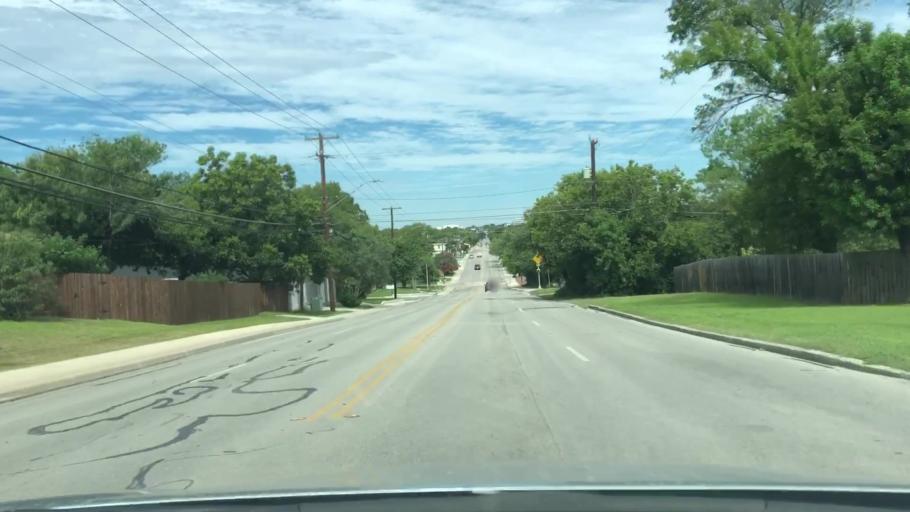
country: US
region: Texas
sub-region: Bexar County
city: Olmos Park
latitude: 29.5014
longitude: -98.4917
